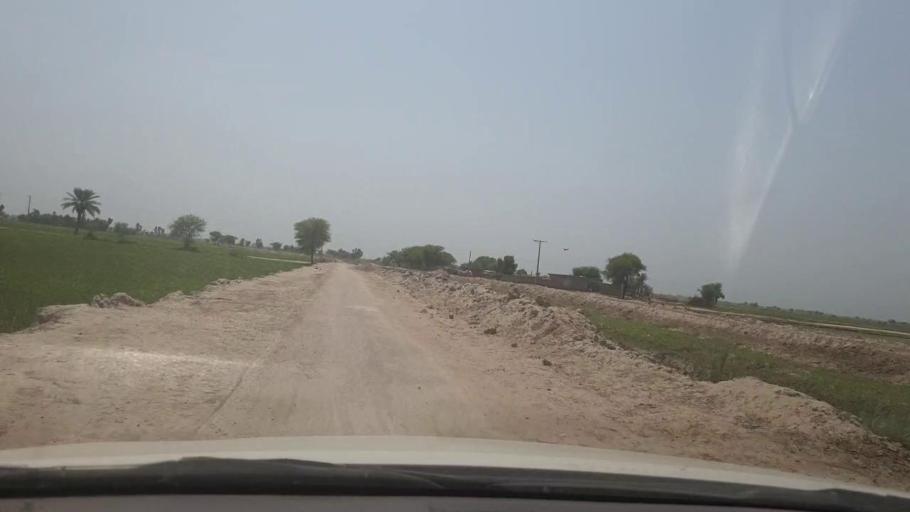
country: PK
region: Sindh
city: Shikarpur
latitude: 28.0423
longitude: 68.5638
